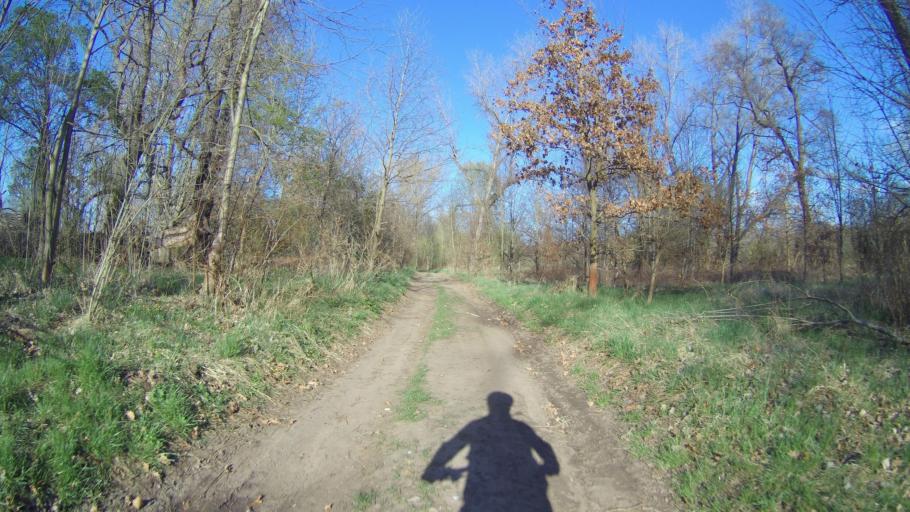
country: CZ
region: Ustecky
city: Zatec
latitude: 50.3359
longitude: 13.5704
